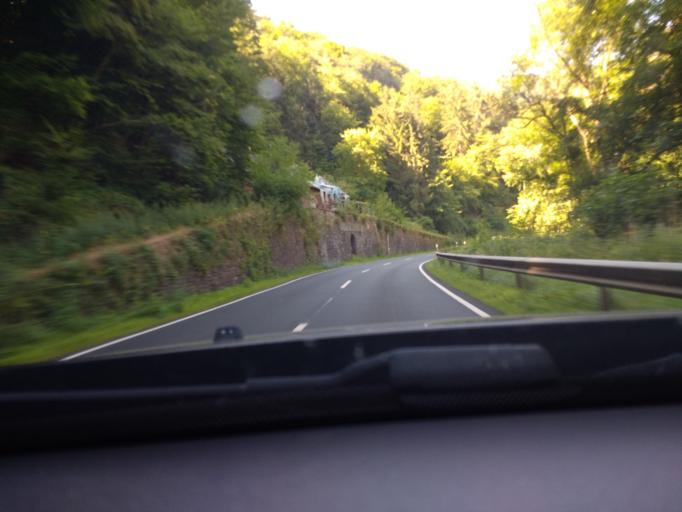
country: DE
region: Rheinland-Pfalz
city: Alf
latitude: 50.0546
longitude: 7.1029
